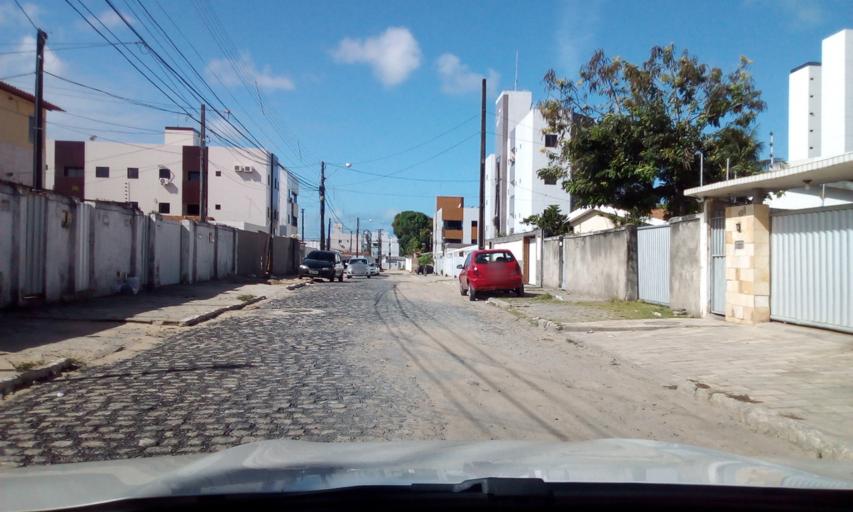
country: BR
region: Paraiba
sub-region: Joao Pessoa
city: Joao Pessoa
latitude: -7.1487
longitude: -34.8399
